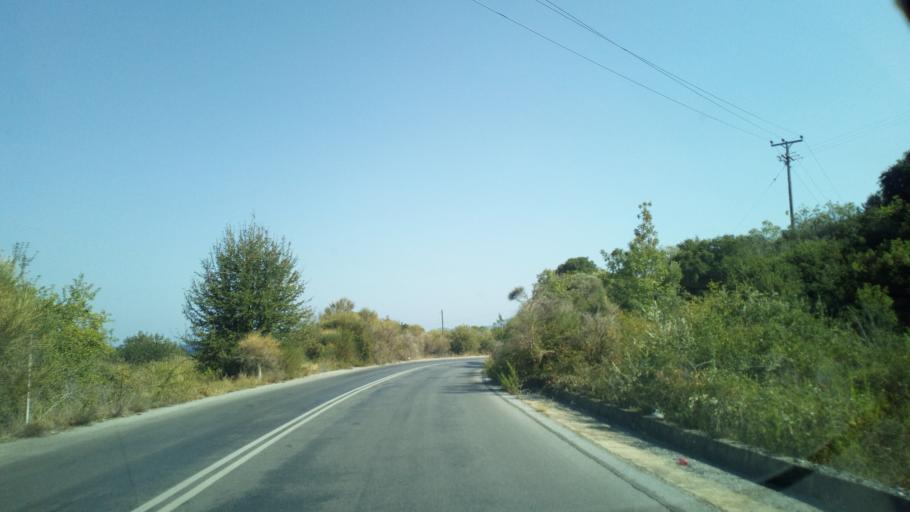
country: GR
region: Central Macedonia
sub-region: Nomos Thessalonikis
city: Stavros
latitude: 40.6157
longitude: 23.7763
